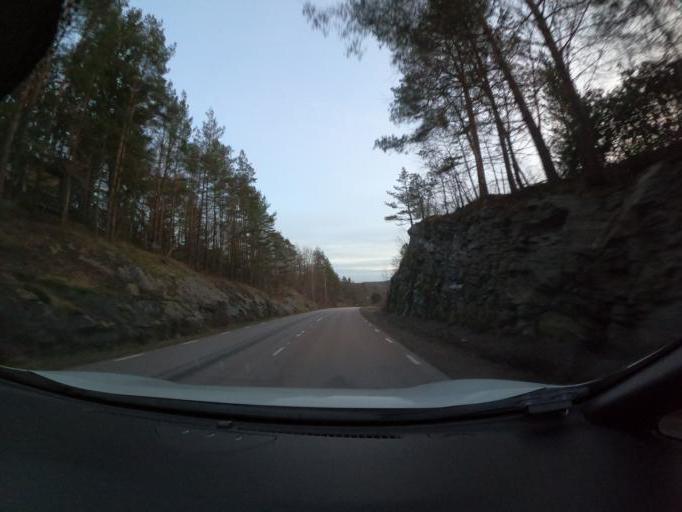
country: SE
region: Vaestra Goetaland
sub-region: Harryda Kommun
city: Molnlycke
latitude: 57.6097
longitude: 12.1795
